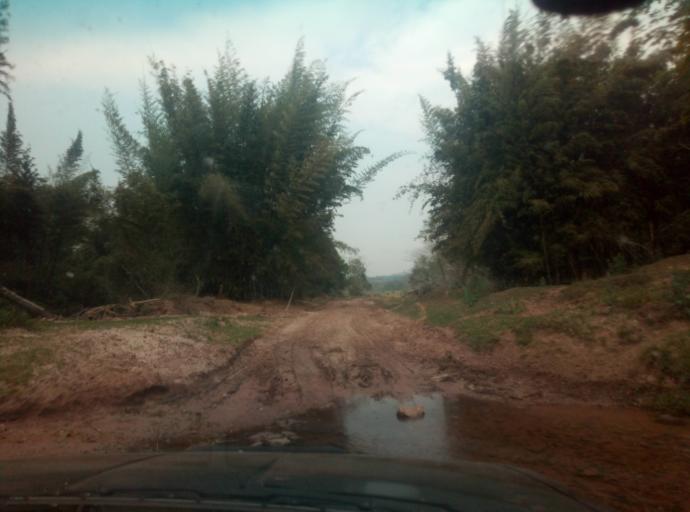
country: PY
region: Caaguazu
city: San Joaquin
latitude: -25.1031
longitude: -56.1218
